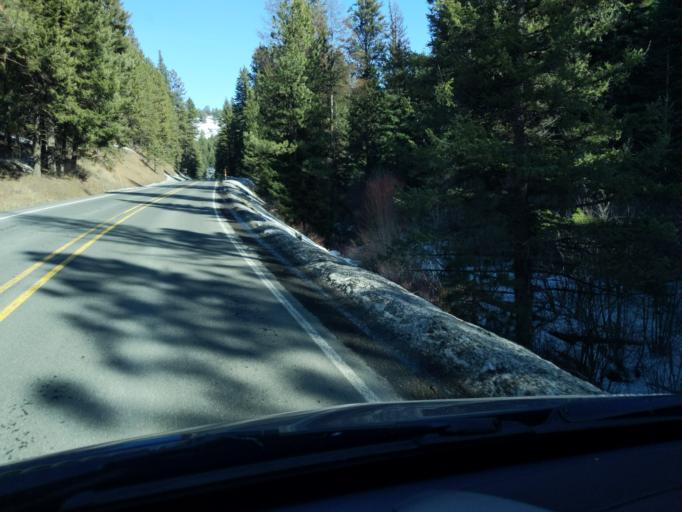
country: US
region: Oregon
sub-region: Grant County
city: John Day
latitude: 44.9400
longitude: -119.0063
